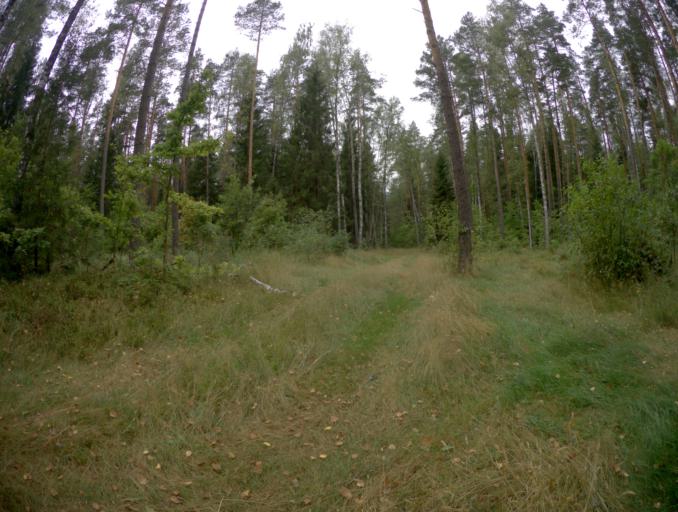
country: RU
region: Vladimir
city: Orgtrud
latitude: 56.1173
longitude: 40.7242
